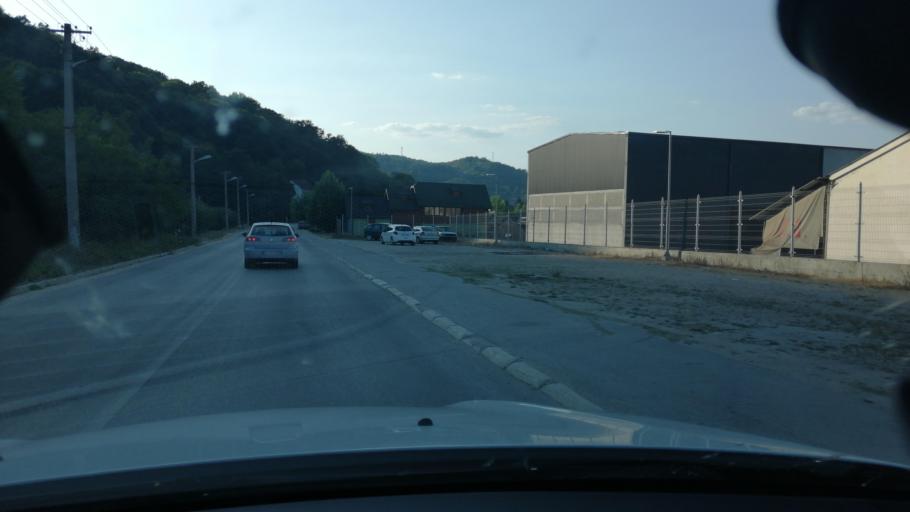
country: RS
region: Central Serbia
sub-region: Moravicki Okrug
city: Lucani
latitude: 43.7700
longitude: 20.2352
